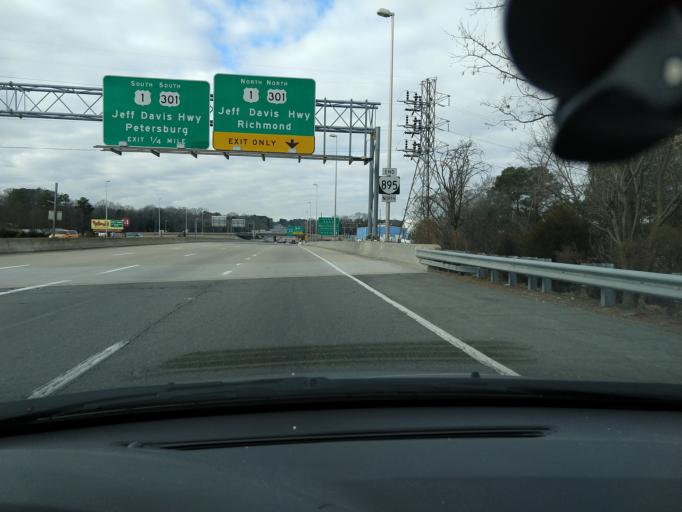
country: US
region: Virginia
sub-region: Chesterfield County
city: Bensley
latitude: 37.4443
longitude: -77.4357
